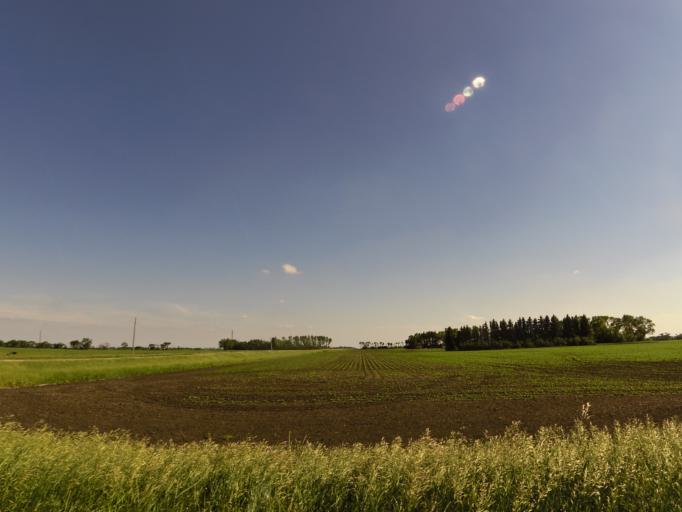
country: US
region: North Dakota
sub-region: Walsh County
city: Grafton
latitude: 48.3534
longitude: -97.2334
